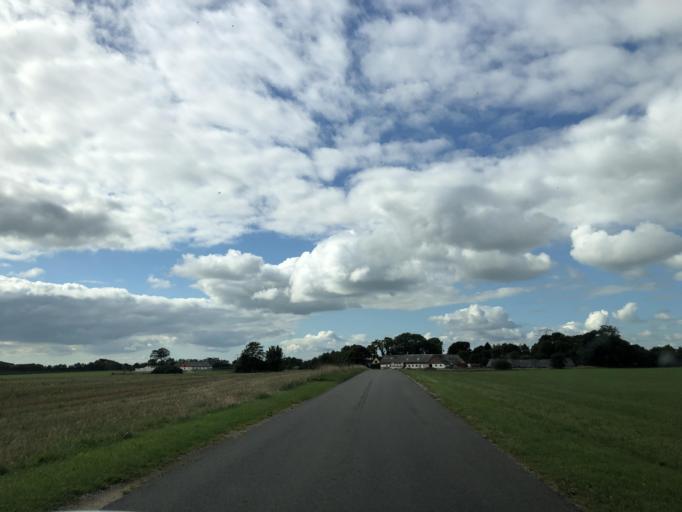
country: DK
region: North Denmark
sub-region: Alborg Kommune
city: Nibe
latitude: 56.8359
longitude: 9.6677
